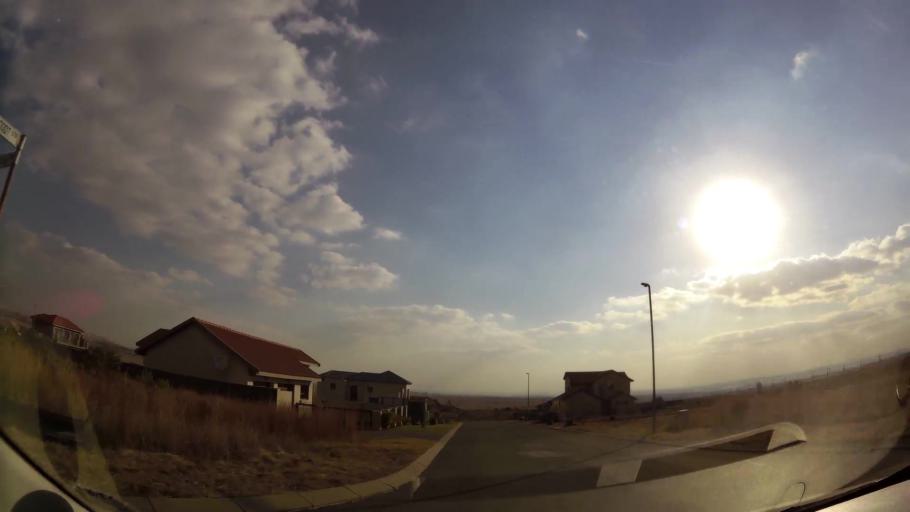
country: ZA
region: Gauteng
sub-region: West Rand District Municipality
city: Krugersdorp
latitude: -26.0993
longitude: 27.7318
